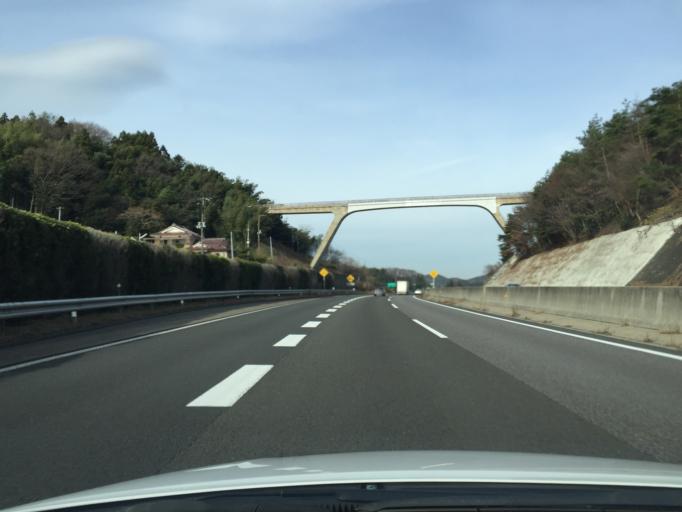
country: JP
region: Fukushima
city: Nihommatsu
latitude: 37.6044
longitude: 140.4216
